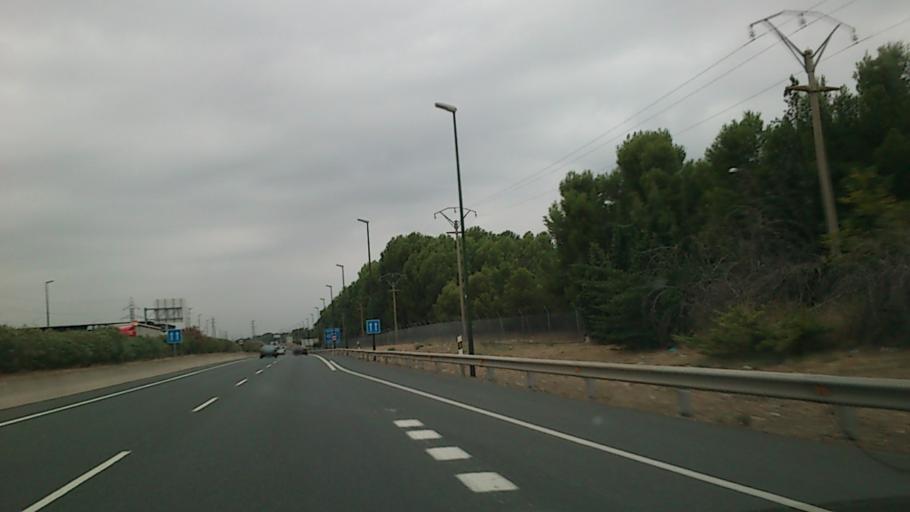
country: ES
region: Aragon
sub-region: Provincia de Zaragoza
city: Zaragoza
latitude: 41.7100
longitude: -0.8621
